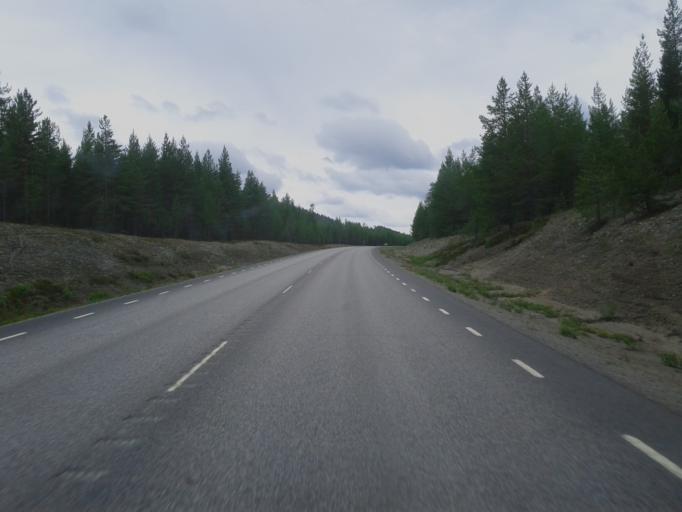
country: SE
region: Vaesterbotten
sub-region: Skelleftea Kommun
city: Langsele
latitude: 64.9206
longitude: 20.0665
